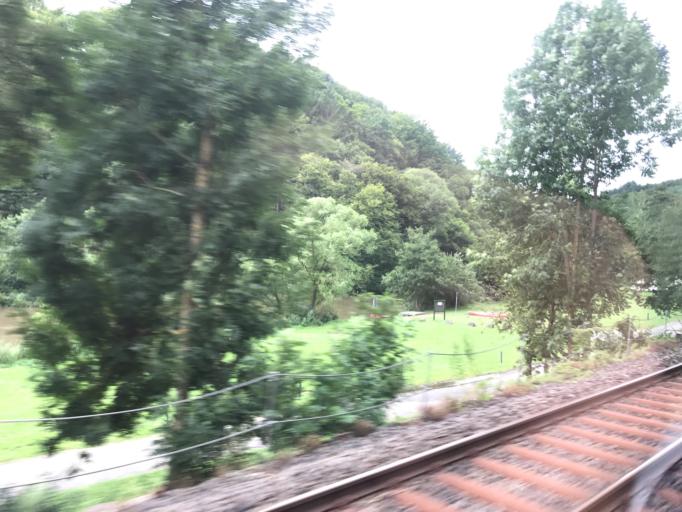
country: DE
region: Hesse
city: Weilburg
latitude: 50.4498
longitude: 8.2527
